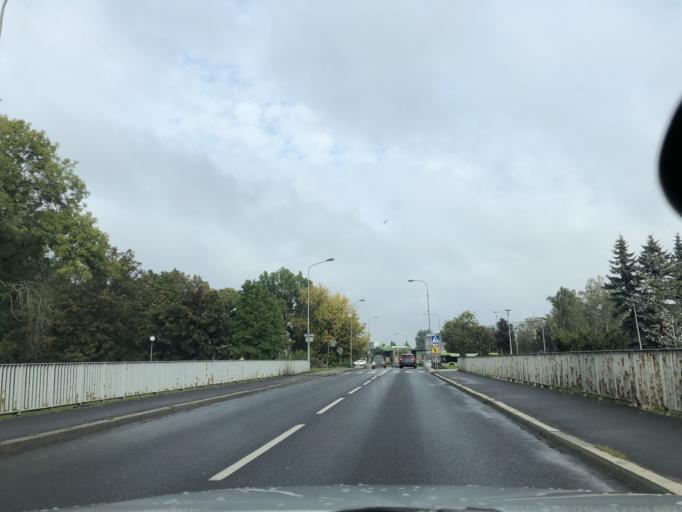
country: PL
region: Greater Poland Voivodeship
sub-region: Powiat pilski
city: Pila
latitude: 53.1506
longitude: 16.7433
